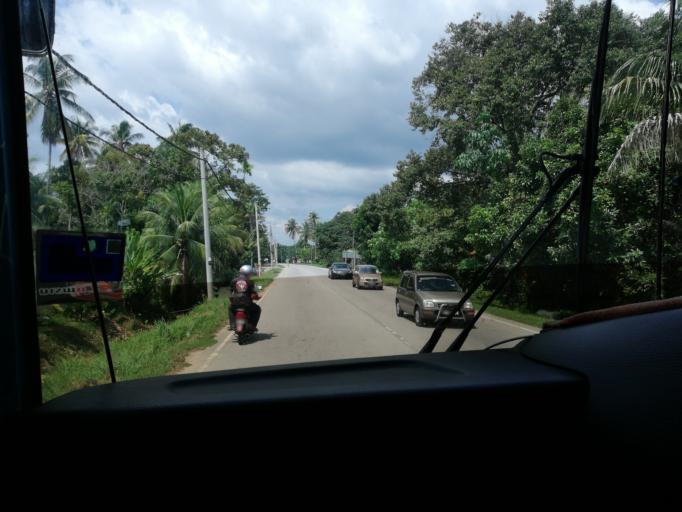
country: MY
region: Perak
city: Parit Buntar
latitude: 5.1169
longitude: 100.5602
